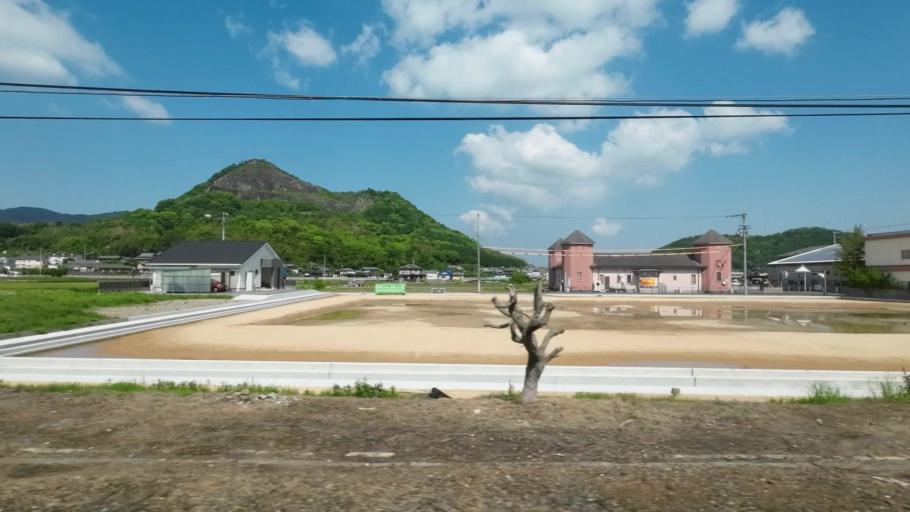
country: JP
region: Kagawa
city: Kan'onjicho
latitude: 34.1852
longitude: 133.7121
